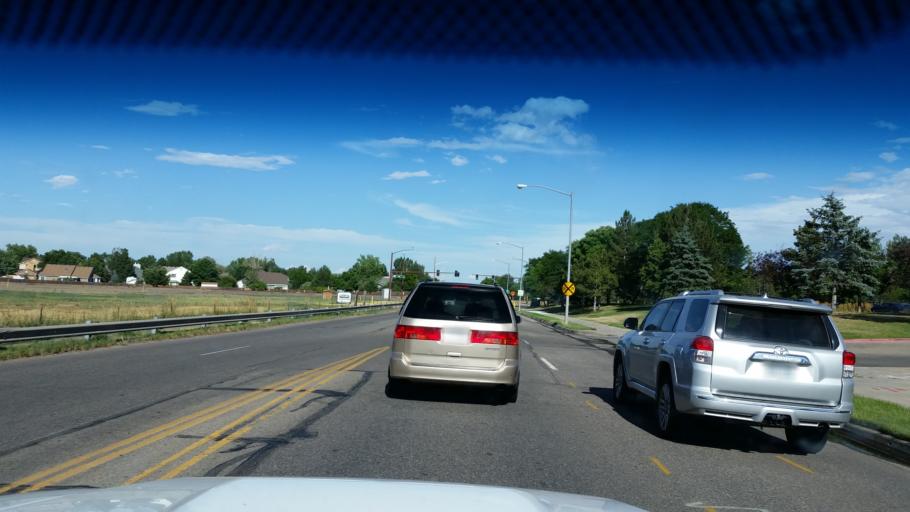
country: US
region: Colorado
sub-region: Adams County
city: Northglenn
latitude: 39.9284
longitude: -104.9678
